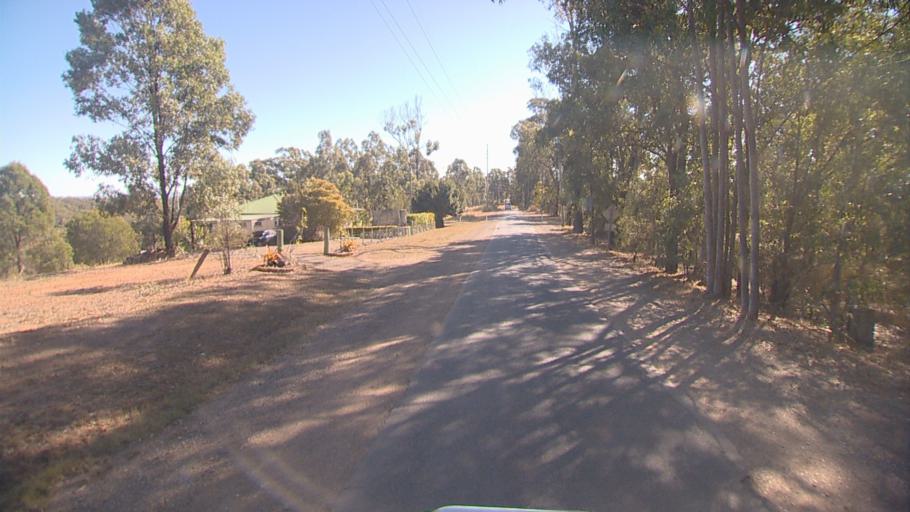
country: AU
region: Queensland
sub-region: Logan
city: Cedar Vale
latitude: -27.8917
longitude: 153.0178
